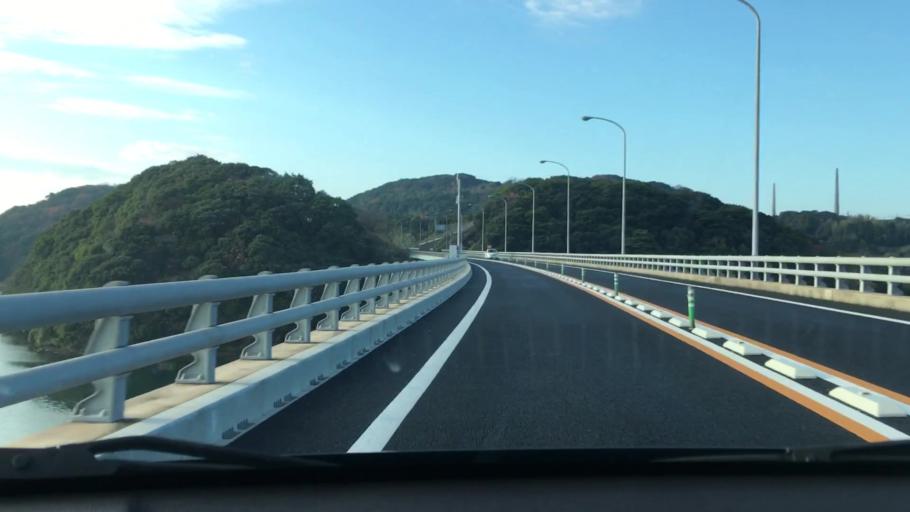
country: JP
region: Nagasaki
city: Sasebo
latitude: 33.0759
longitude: 129.7686
